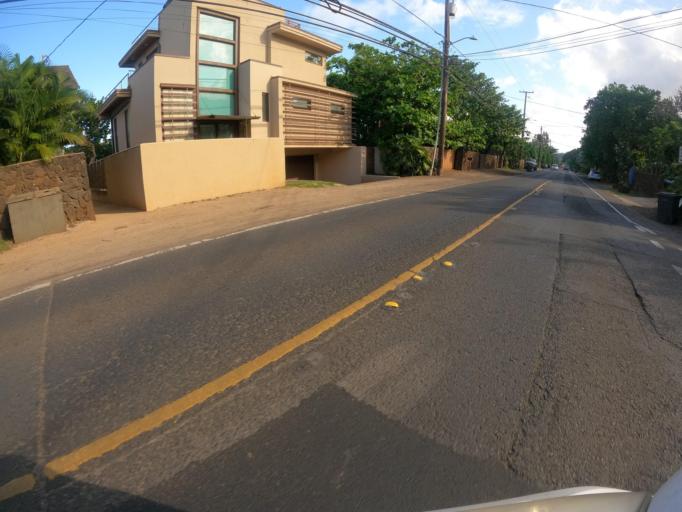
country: US
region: Hawaii
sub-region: Honolulu County
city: Pupukea
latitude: 21.6303
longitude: -158.0717
